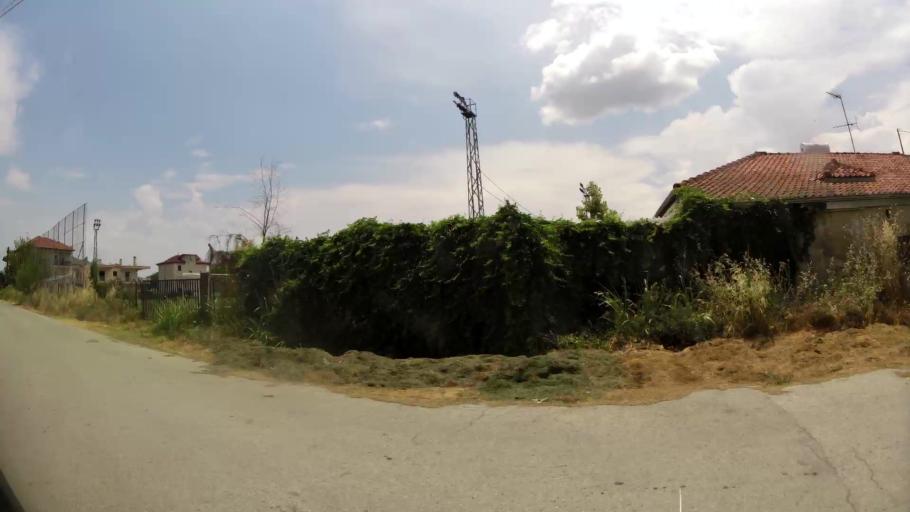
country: GR
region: Central Macedonia
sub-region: Nomos Pierias
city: Peristasi
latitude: 40.2752
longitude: 22.5452
